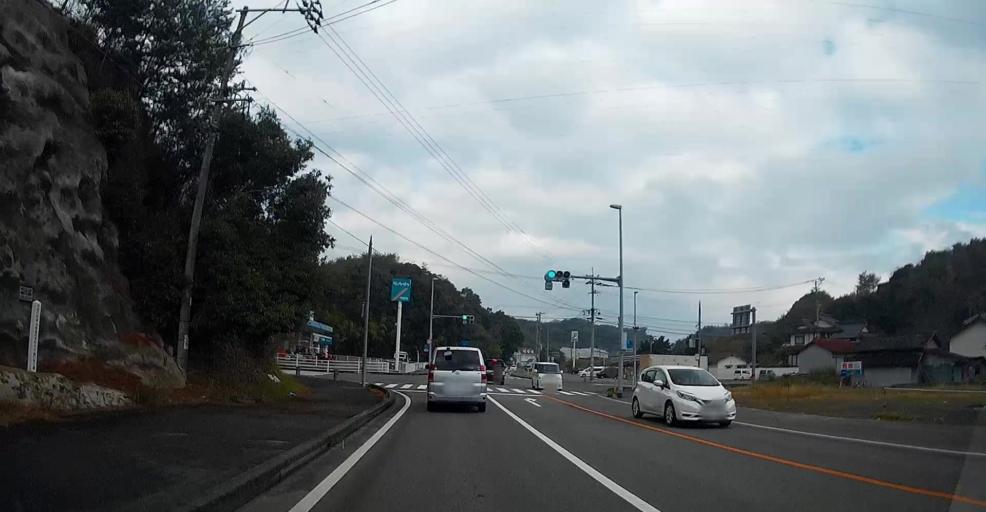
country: JP
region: Kumamoto
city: Yatsushiro
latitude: 32.5522
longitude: 130.4182
